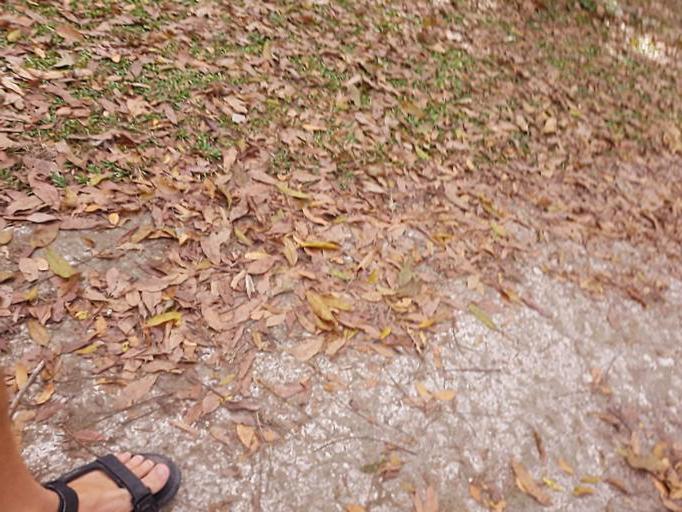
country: GT
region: Peten
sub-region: Municipio de San Jose
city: San Jose
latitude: 17.2197
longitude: -89.6259
